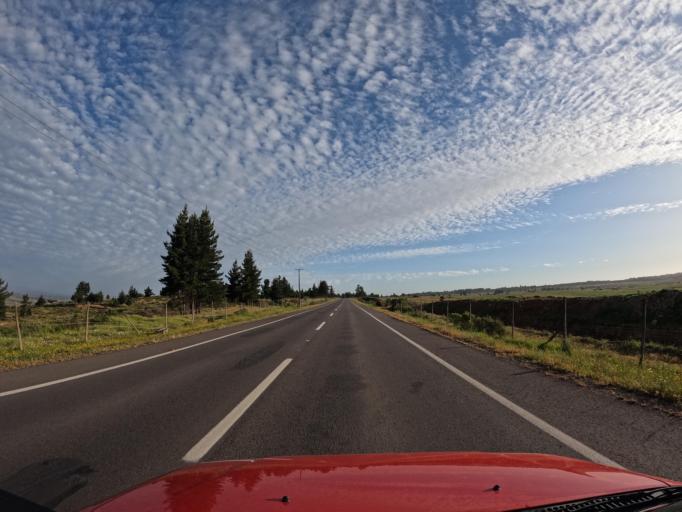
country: CL
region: Valparaiso
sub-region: San Antonio Province
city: San Antonio
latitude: -34.0610
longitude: -71.6261
